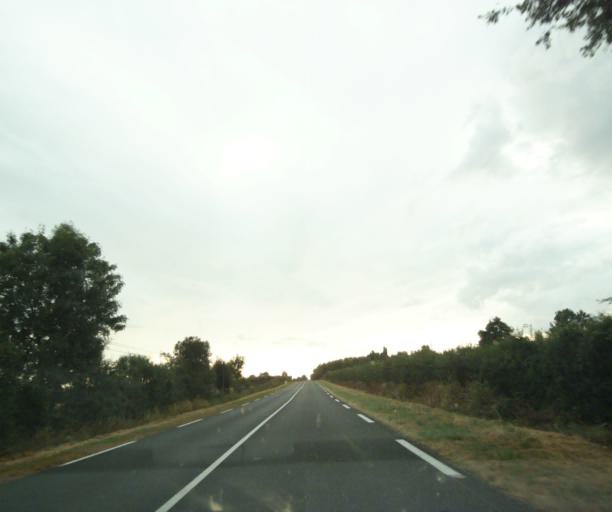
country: FR
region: Pays de la Loire
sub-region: Departement de la Vendee
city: Avrille
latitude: 46.4649
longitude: -1.4675
